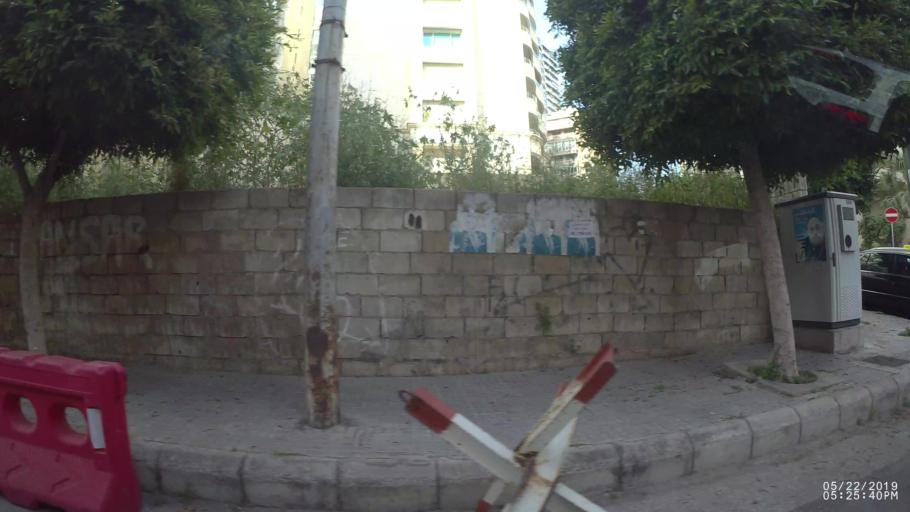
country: LB
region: Beyrouth
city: Ra's Bayrut
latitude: 33.8892
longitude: 35.4752
